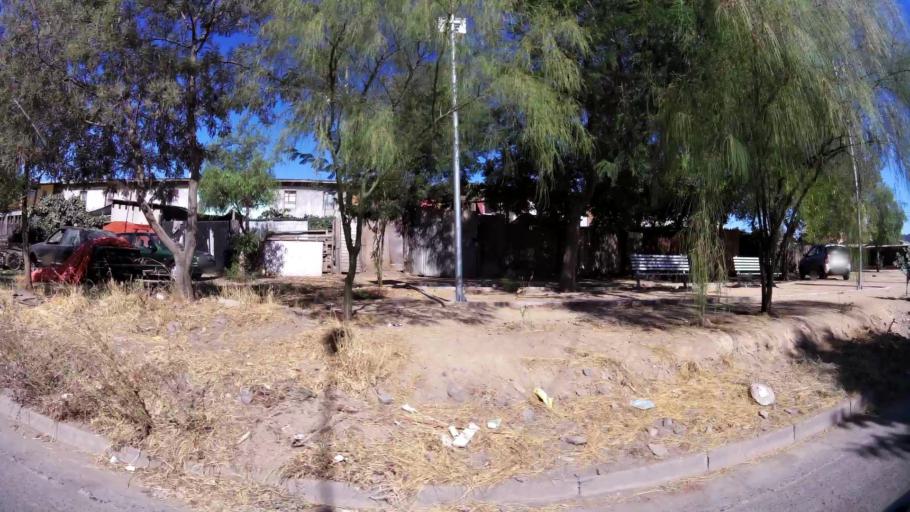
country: CL
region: O'Higgins
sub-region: Provincia de Colchagua
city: Chimbarongo
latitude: -34.5913
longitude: -71.0005
